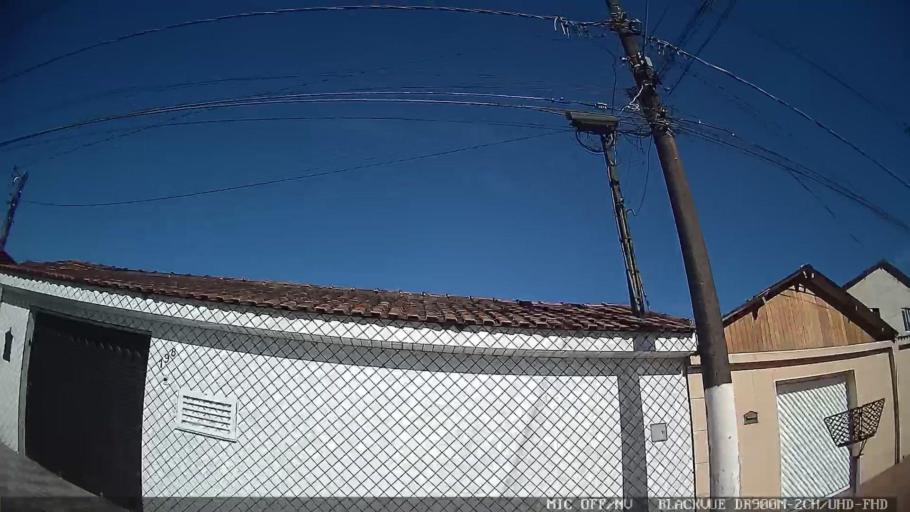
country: BR
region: Sao Paulo
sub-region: Santos
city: Santos
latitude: -23.9356
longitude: -46.2884
